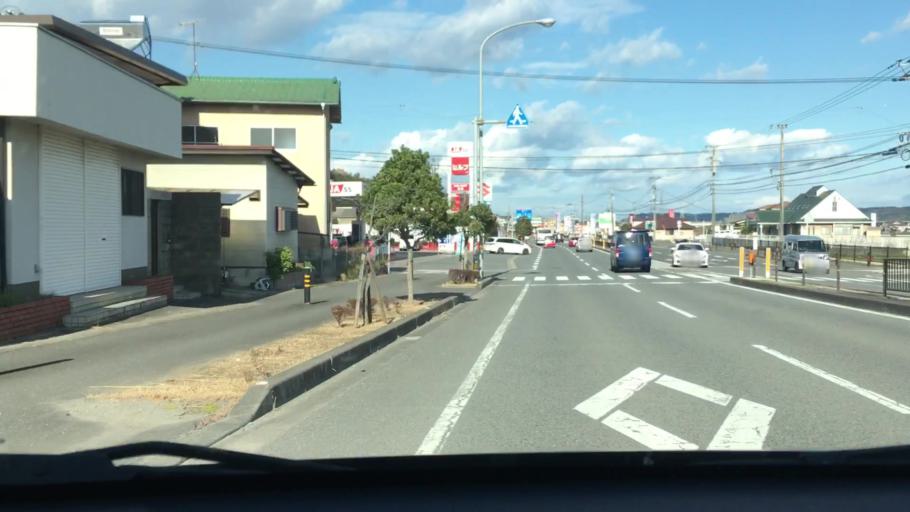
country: JP
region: Oita
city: Tsurusaki
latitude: 33.1880
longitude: 131.6703
